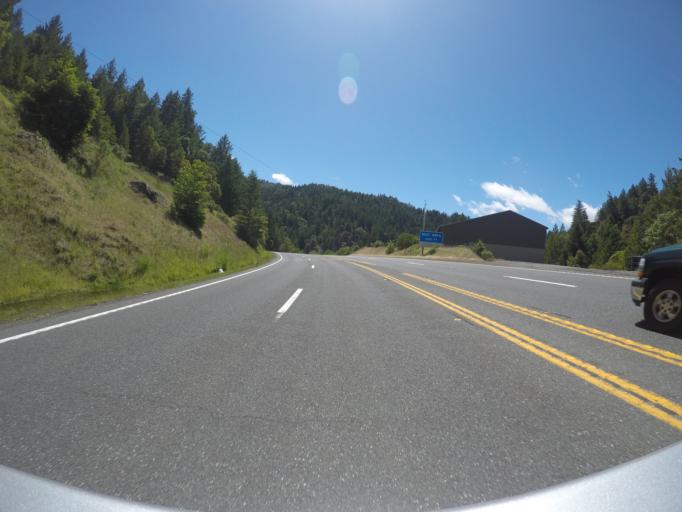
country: US
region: California
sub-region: Mendocino County
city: Laytonville
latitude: 39.8276
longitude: -123.5899
